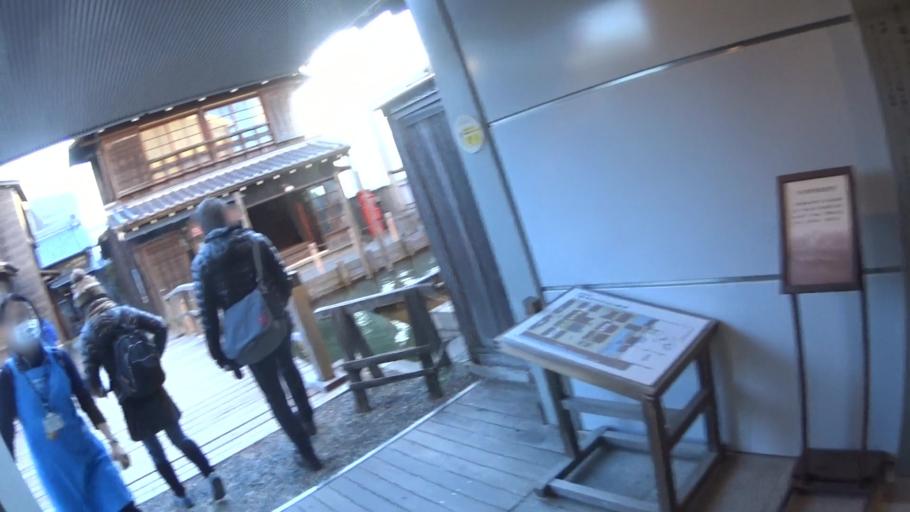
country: JP
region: Tokyo
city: Urayasu
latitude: 35.6575
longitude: 139.9010
